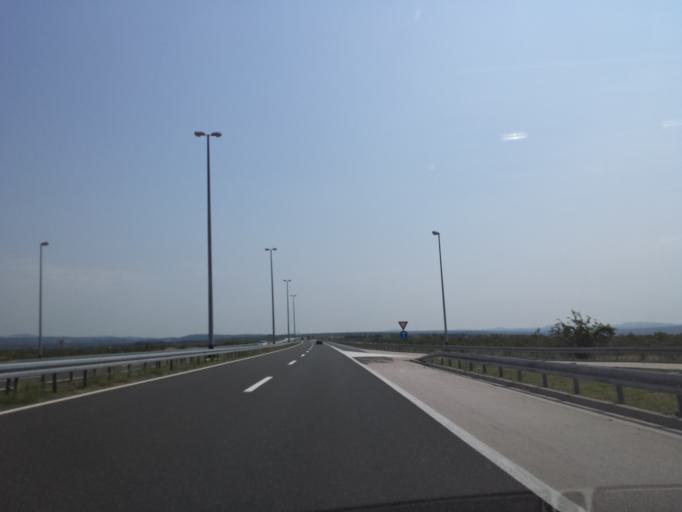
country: HR
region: Zadarska
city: Polaca
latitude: 44.0608
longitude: 15.5322
